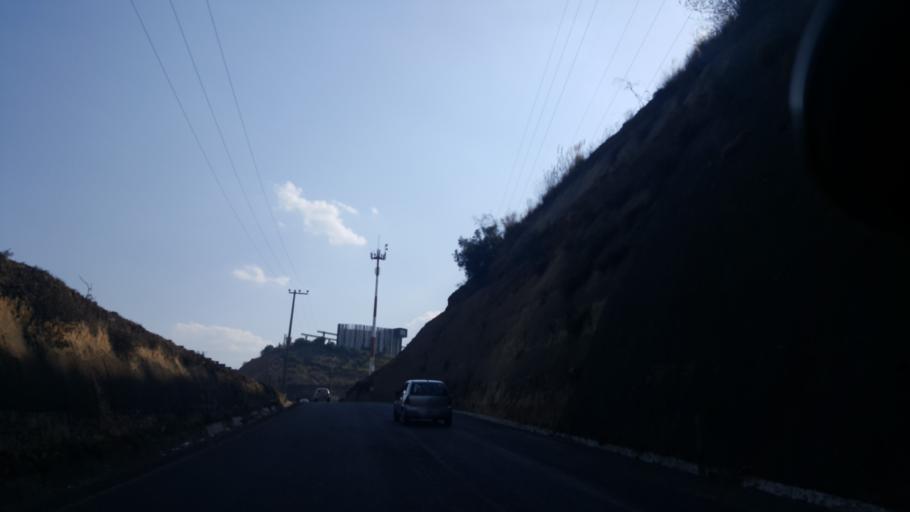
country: MX
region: Mexico
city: Ciudad Lopez Mateos
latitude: 19.5806
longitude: -99.2692
